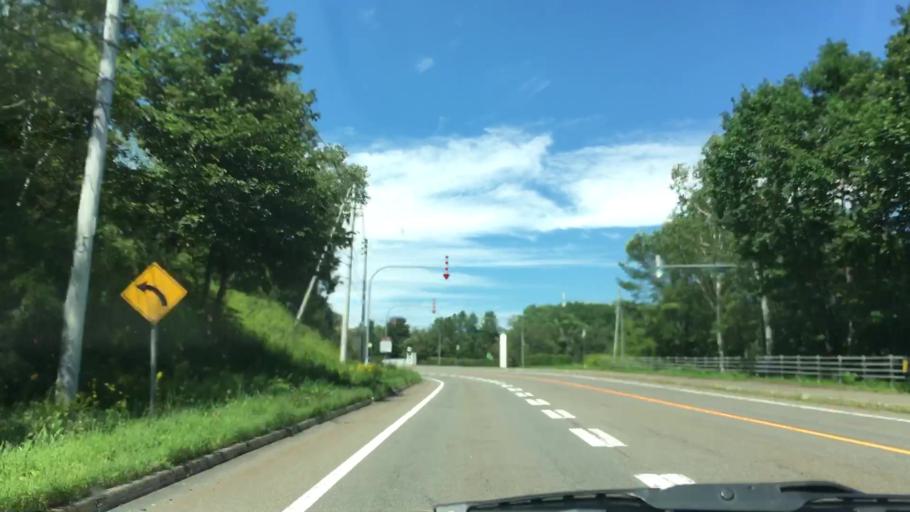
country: JP
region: Hokkaido
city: Otofuke
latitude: 43.2370
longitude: 143.5385
